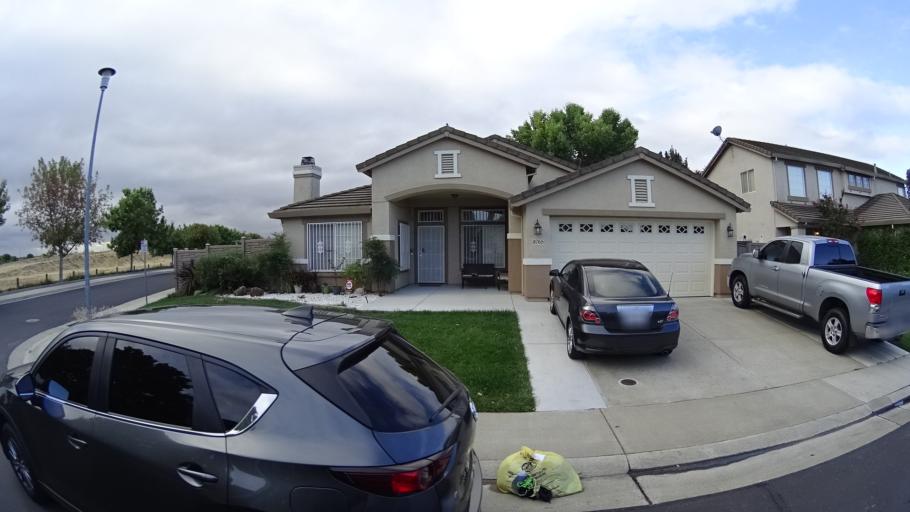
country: US
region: California
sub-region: Sacramento County
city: Laguna
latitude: 38.4376
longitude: -121.4249
